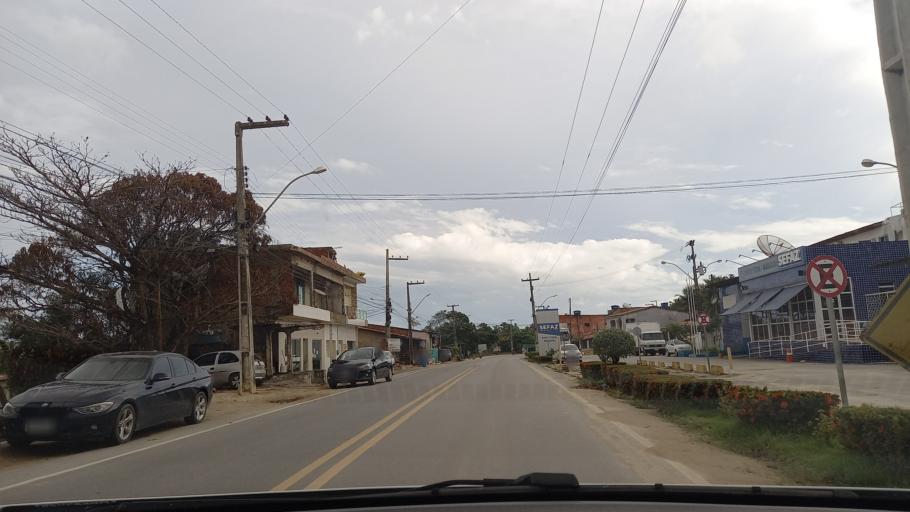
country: BR
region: Alagoas
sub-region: Maragogi
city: Maragogi
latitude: -8.9841
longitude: -35.1965
